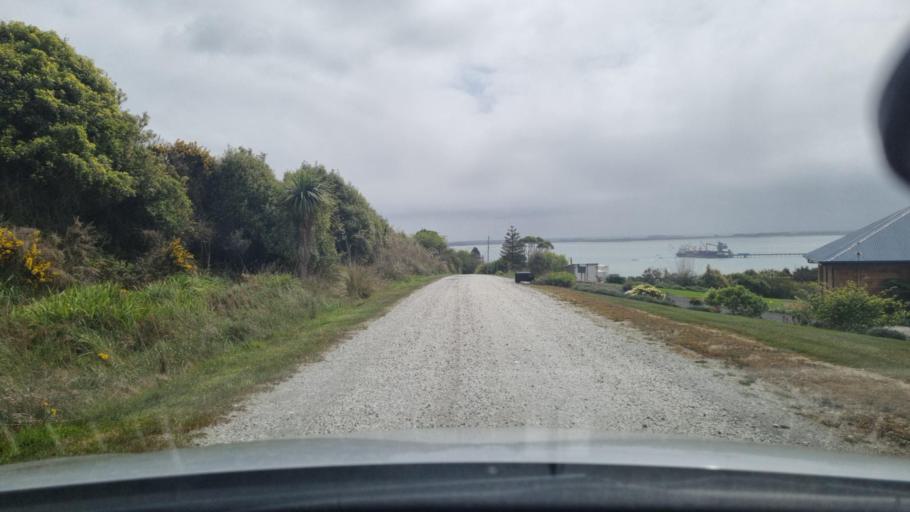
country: NZ
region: Southland
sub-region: Invercargill City
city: Bluff
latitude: -46.6085
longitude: 168.3516
